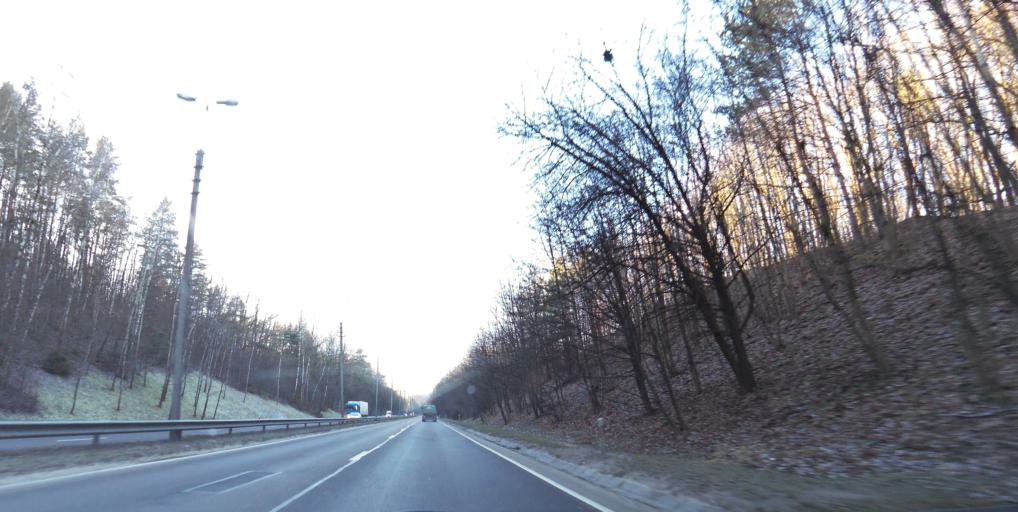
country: LT
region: Vilnius County
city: Lazdynai
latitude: 54.6422
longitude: 25.1996
